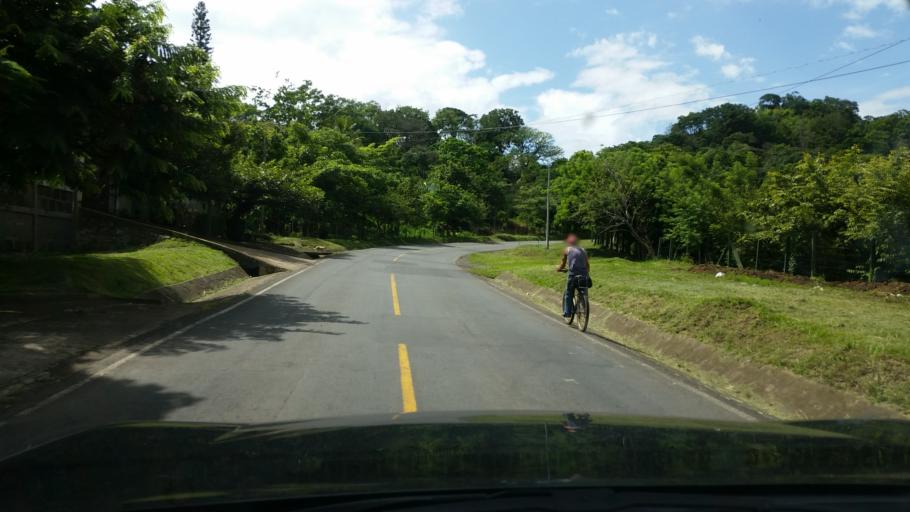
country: NI
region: Matagalpa
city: San Ramon
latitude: 12.9523
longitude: -85.8714
